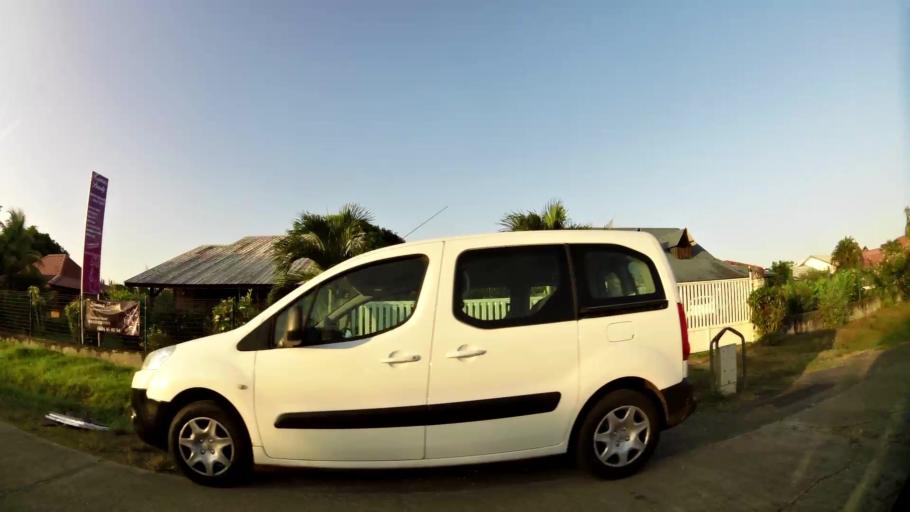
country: GF
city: Macouria
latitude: 5.0084
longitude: -52.4691
